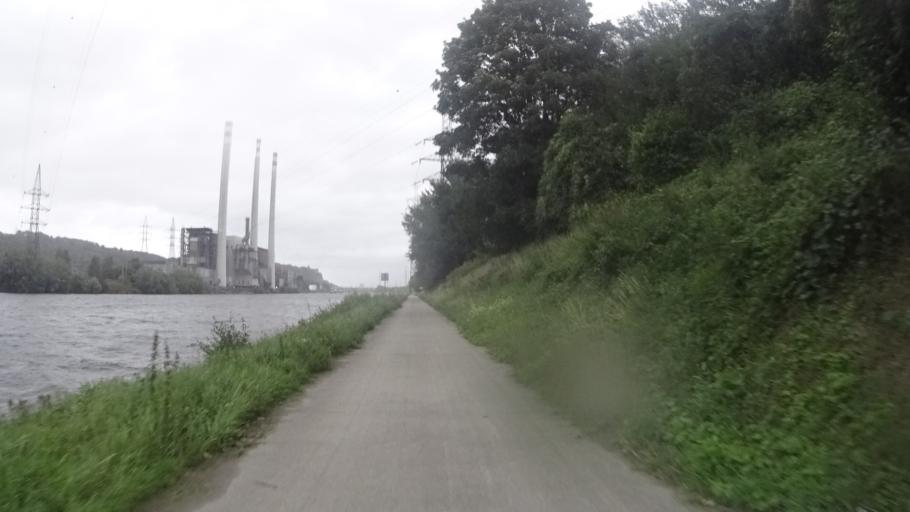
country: BE
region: Wallonia
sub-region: Province de Liege
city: Engis
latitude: 50.5820
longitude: 5.4118
